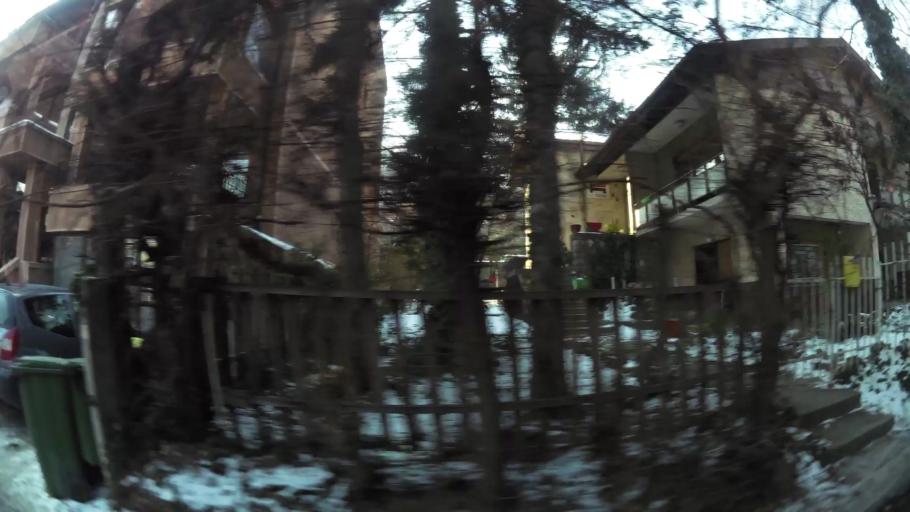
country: MK
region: Karpos
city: Skopje
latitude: 41.9836
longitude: 21.4263
